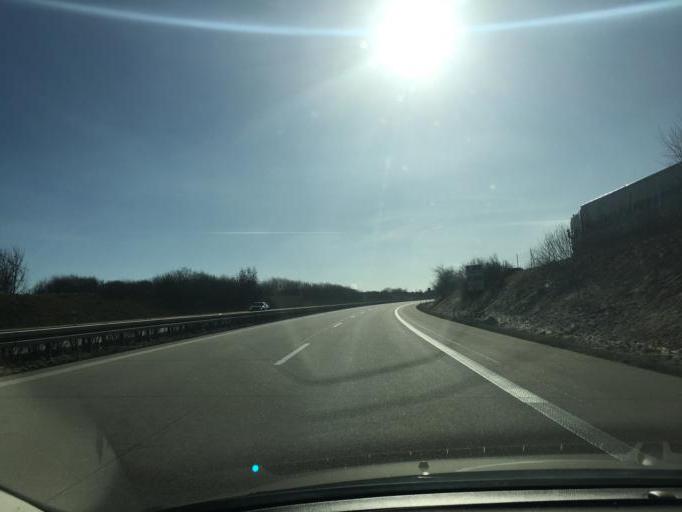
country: DE
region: Saxony
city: Muhlau
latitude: 50.8855
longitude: 12.7729
